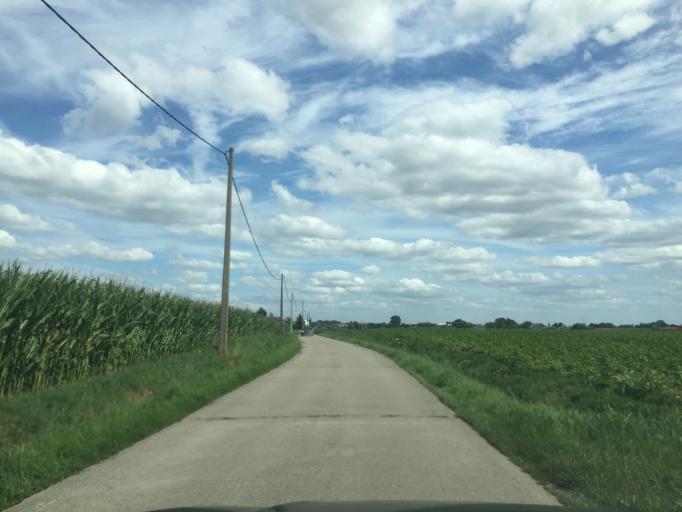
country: BE
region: Flanders
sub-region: Provincie West-Vlaanderen
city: Staden
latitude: 50.9891
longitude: 3.0368
